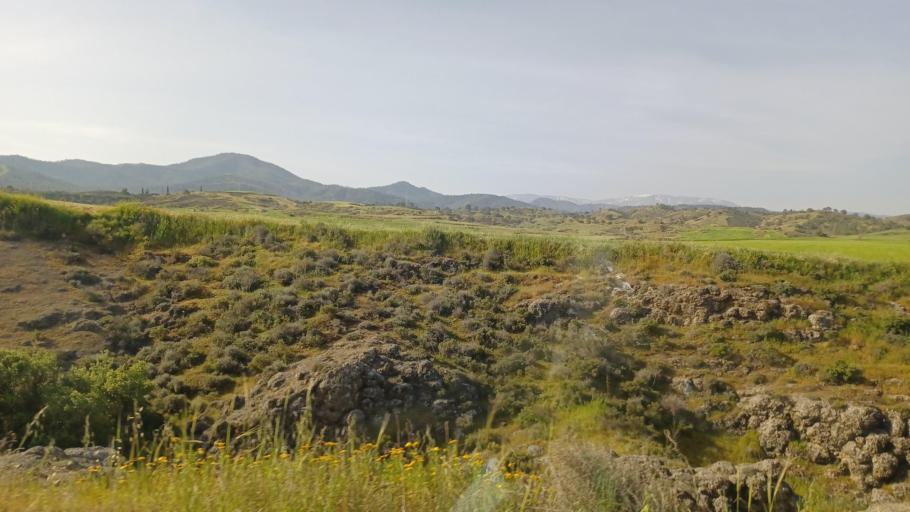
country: CY
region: Lefkosia
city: Lefka
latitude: 35.0891
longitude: 32.9471
